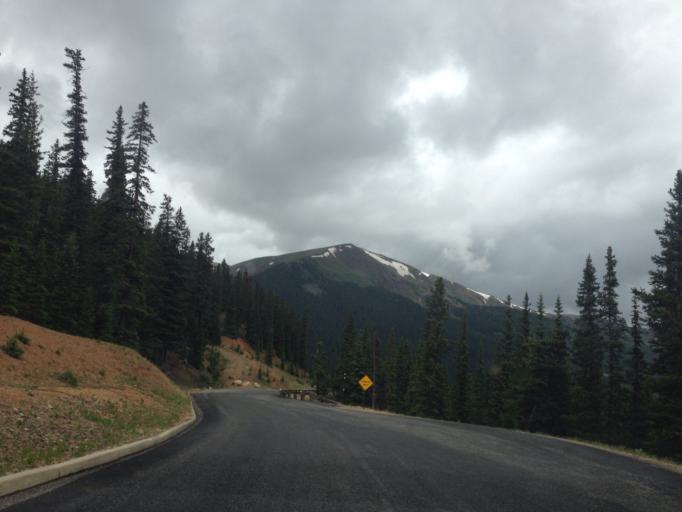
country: US
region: Colorado
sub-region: Clear Creek County
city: Georgetown
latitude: 39.6023
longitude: -105.7102
